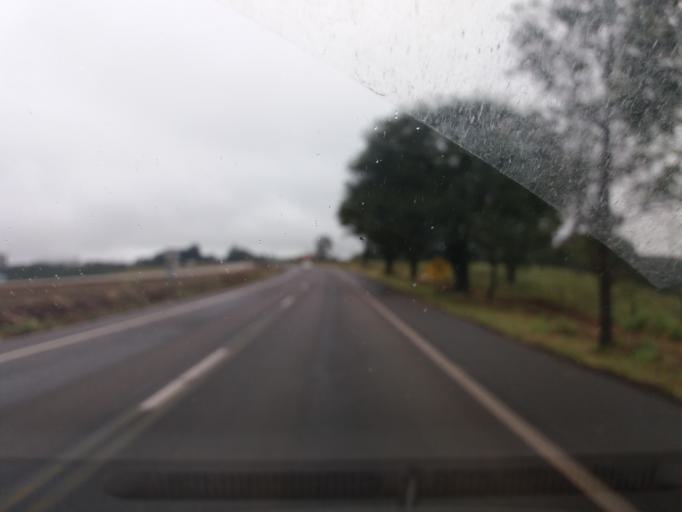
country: BR
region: Parana
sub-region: Cascavel
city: Cascavel
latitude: -25.1706
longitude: -53.6021
